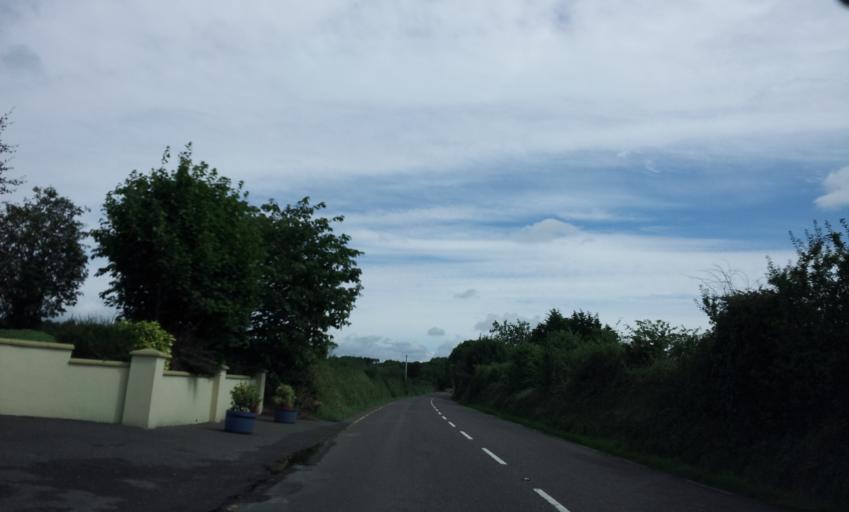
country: IE
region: Munster
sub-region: Ciarrai
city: Killorglin
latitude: 52.1015
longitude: -9.7690
